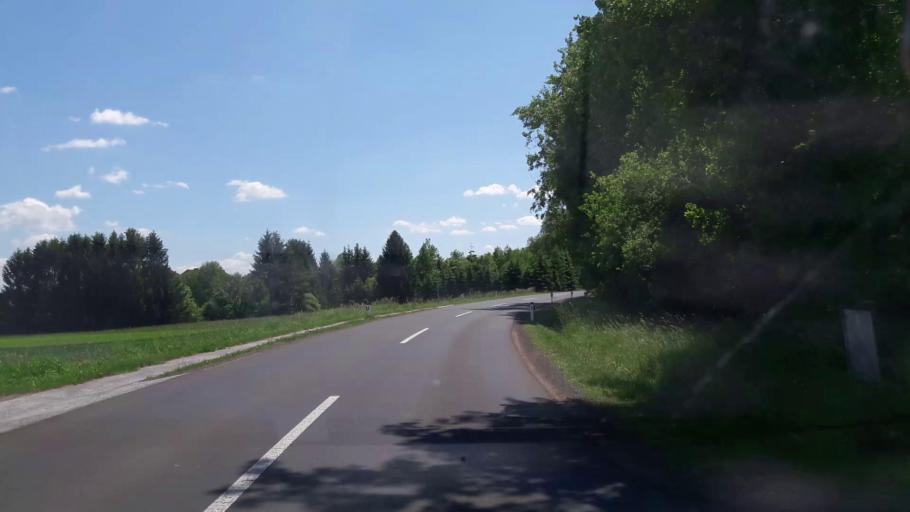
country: AT
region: Burgenland
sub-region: Politischer Bezirk Jennersdorf
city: Jennersdorf
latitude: 46.9419
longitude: 16.1311
